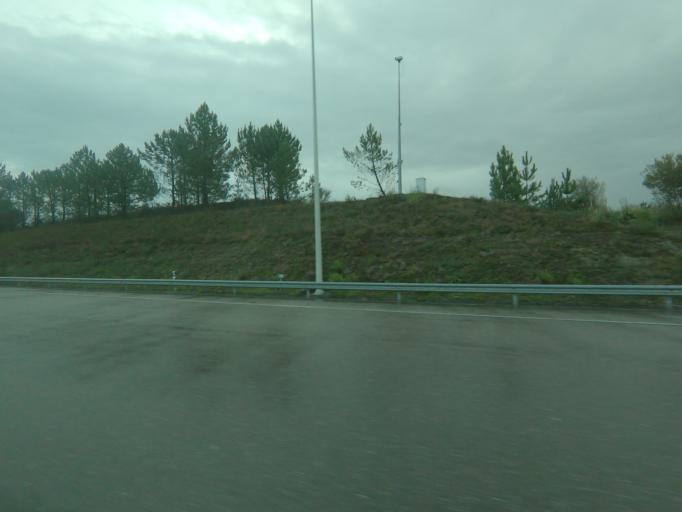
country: PT
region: Viana do Castelo
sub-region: Valenca
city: Valenza
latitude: 41.9778
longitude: -8.6556
